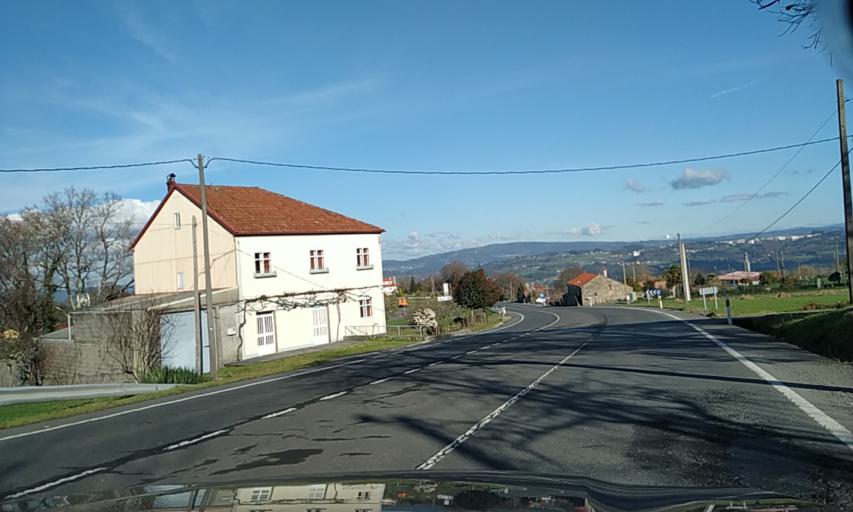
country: ES
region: Galicia
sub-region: Provincia de Pontevedra
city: Silleda
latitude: 42.6986
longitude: -8.3208
